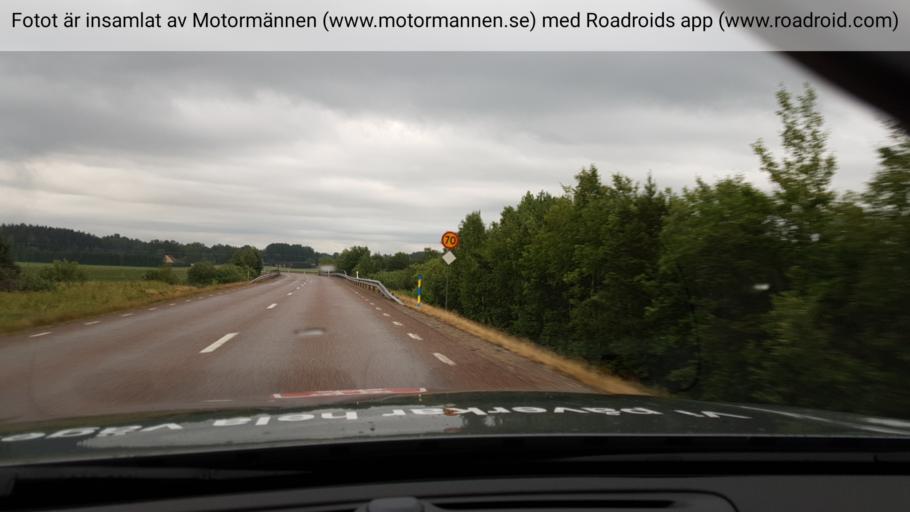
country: SE
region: Vaestmanland
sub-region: Surahammars Kommun
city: Ramnas
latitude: 59.9085
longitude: 16.3304
